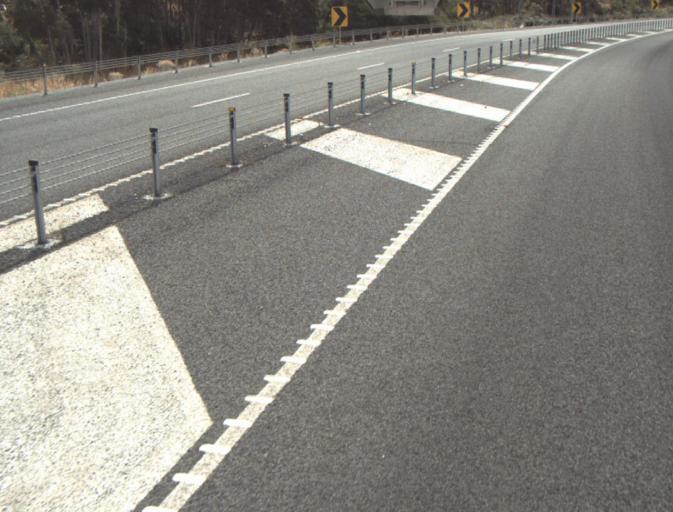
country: AU
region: Tasmania
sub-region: Launceston
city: Mayfield
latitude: -41.3001
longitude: 147.0496
